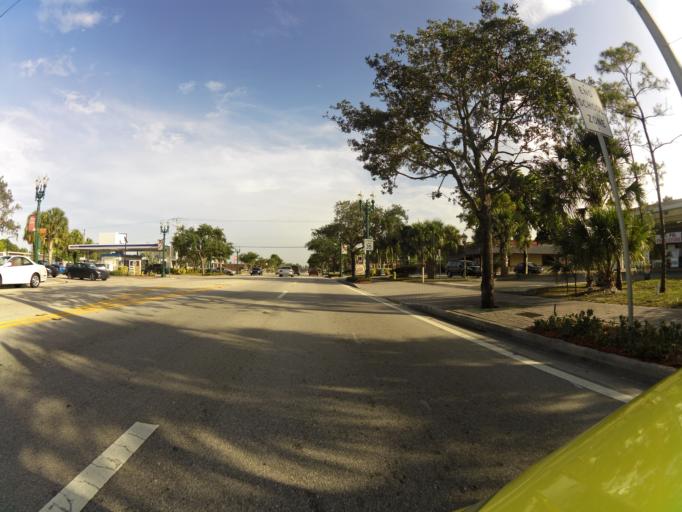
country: US
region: Florida
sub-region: Broward County
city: Davie
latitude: 26.0729
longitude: -80.2324
